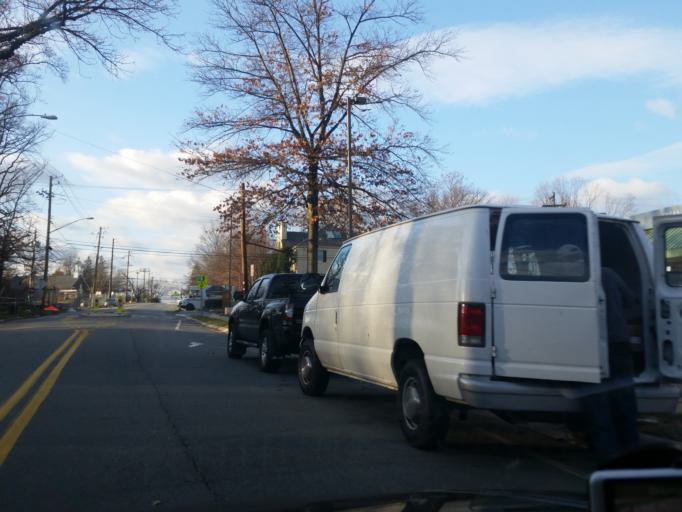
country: US
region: Maryland
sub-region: Montgomery County
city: Forest Glen
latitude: 38.9922
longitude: -77.0492
